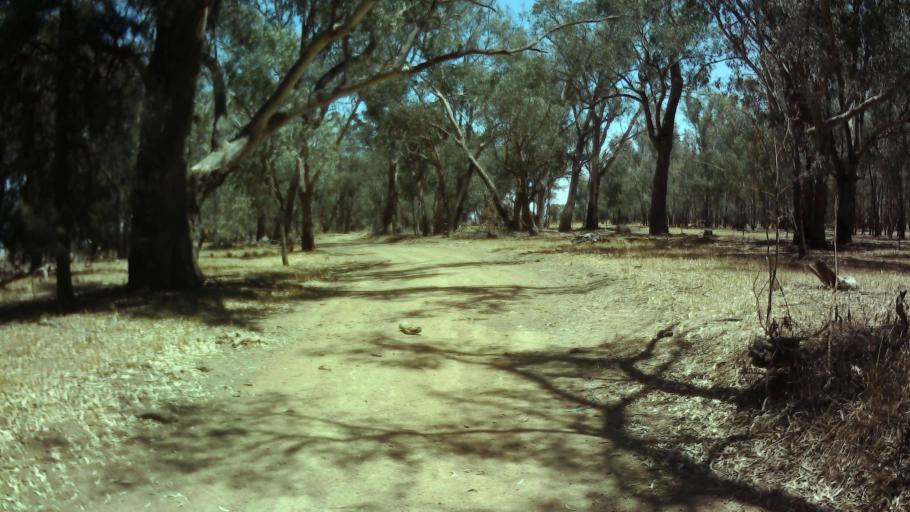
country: AU
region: New South Wales
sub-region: Weddin
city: Grenfell
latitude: -34.0464
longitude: 147.8358
